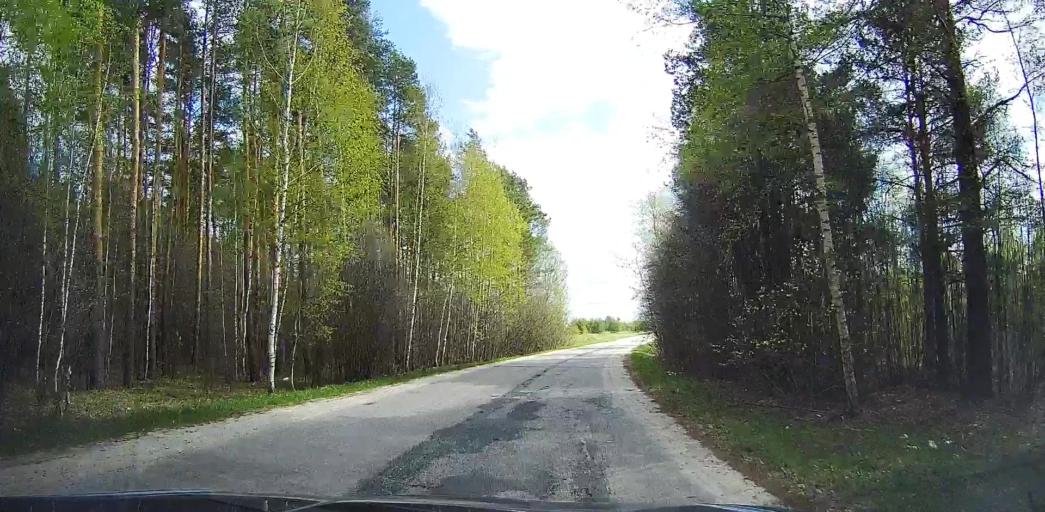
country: RU
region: Moskovskaya
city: Davydovo
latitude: 55.6441
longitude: 38.7735
